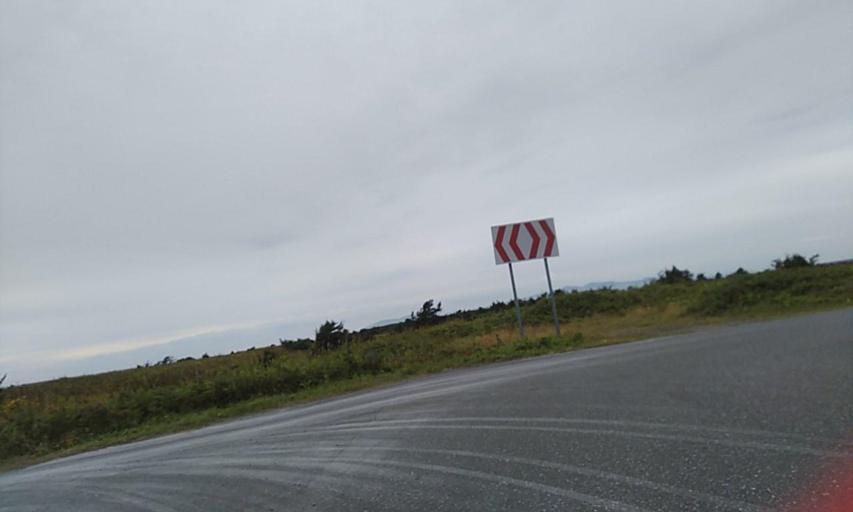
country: JP
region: Hokkaido
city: Makubetsu
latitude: 45.2377
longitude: 142.2681
